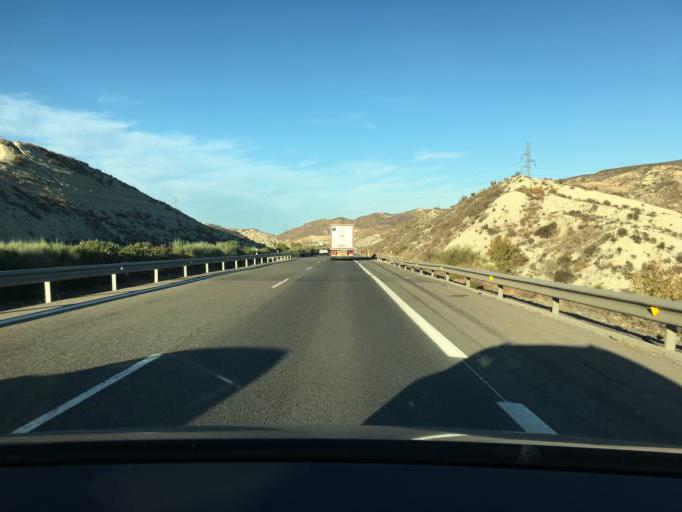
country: ES
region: Andalusia
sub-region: Provincia de Almeria
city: Sorbas
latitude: 37.0959
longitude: -2.0471
